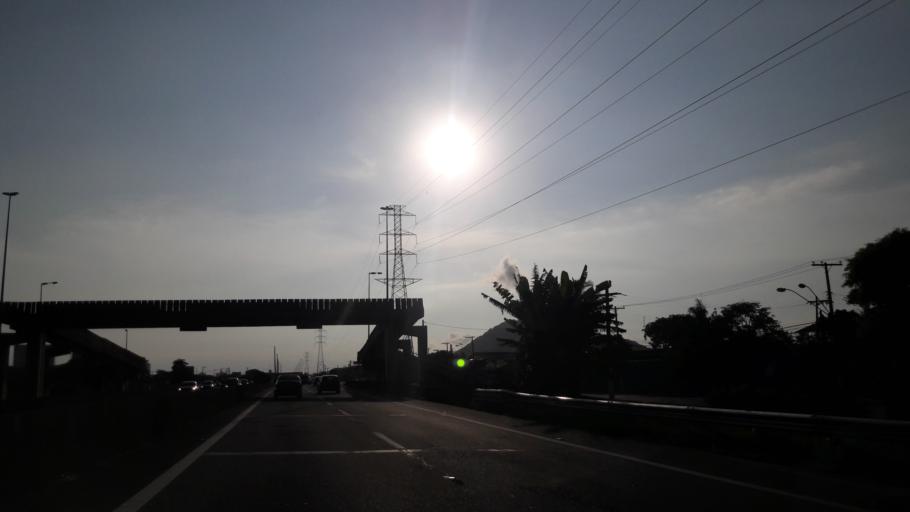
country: BR
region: Sao Paulo
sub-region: Mongagua
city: Mongagua
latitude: -24.1108
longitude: -46.6557
